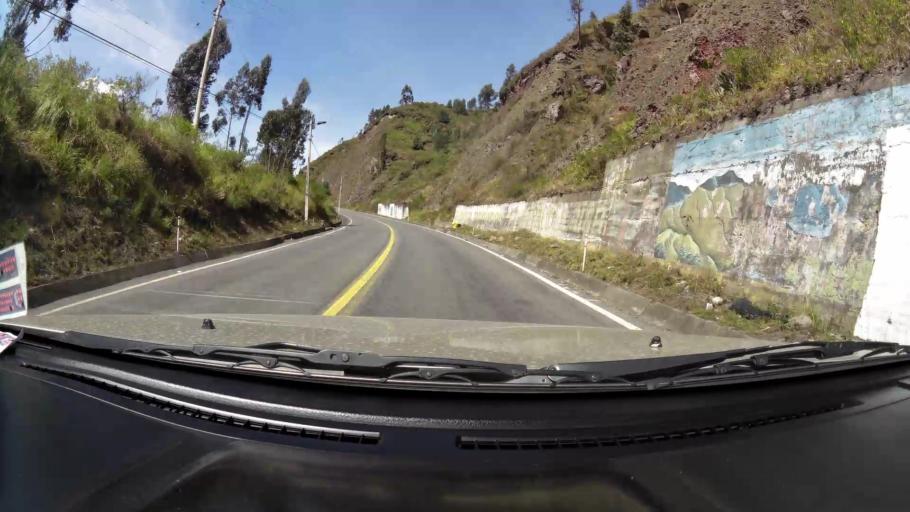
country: EC
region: Chimborazo
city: Guano
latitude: -1.5712
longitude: -78.5345
